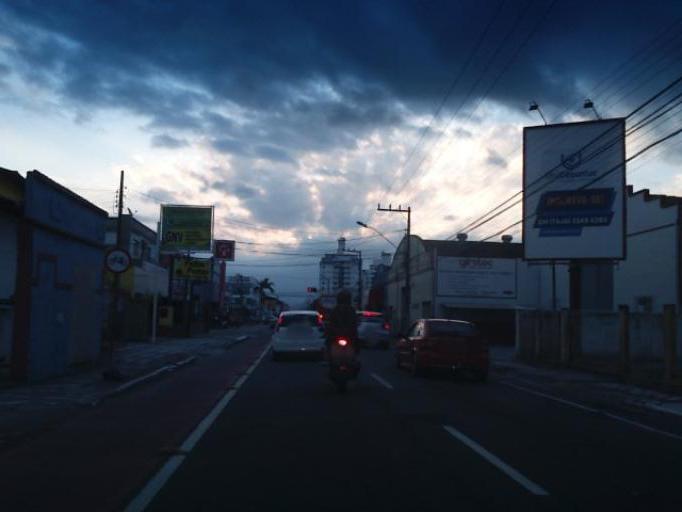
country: BR
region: Santa Catarina
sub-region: Itajai
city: Itajai
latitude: -26.9080
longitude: -48.6764
